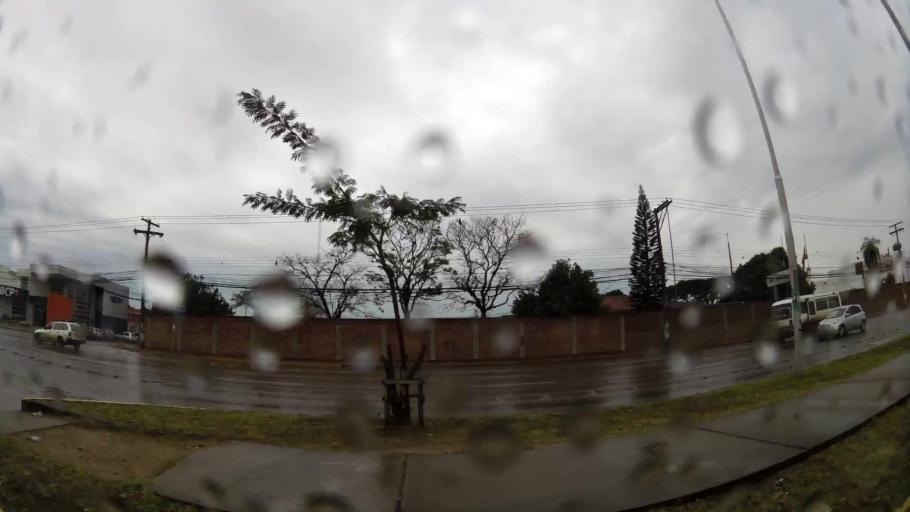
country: BO
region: Santa Cruz
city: Santa Cruz de la Sierra
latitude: -17.8086
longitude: -63.2044
